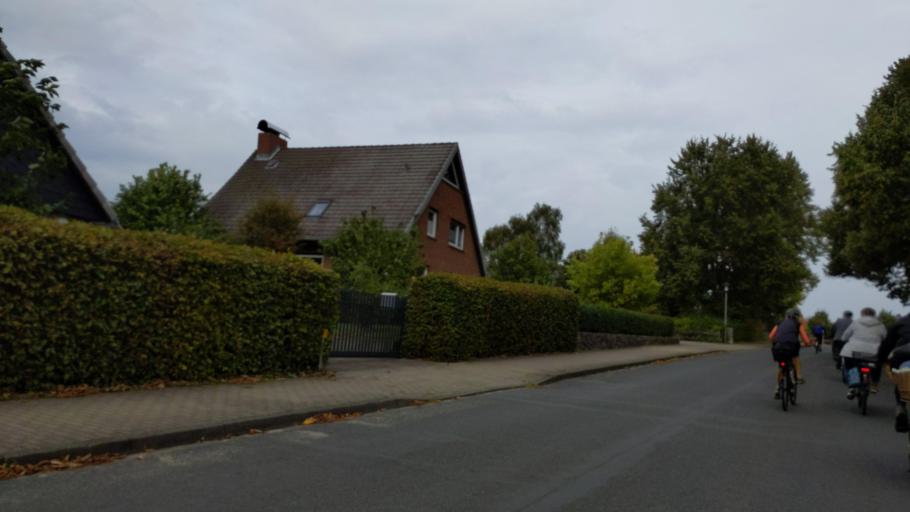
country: DE
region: Schleswig-Holstein
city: Bak
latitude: 53.7150
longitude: 10.7867
